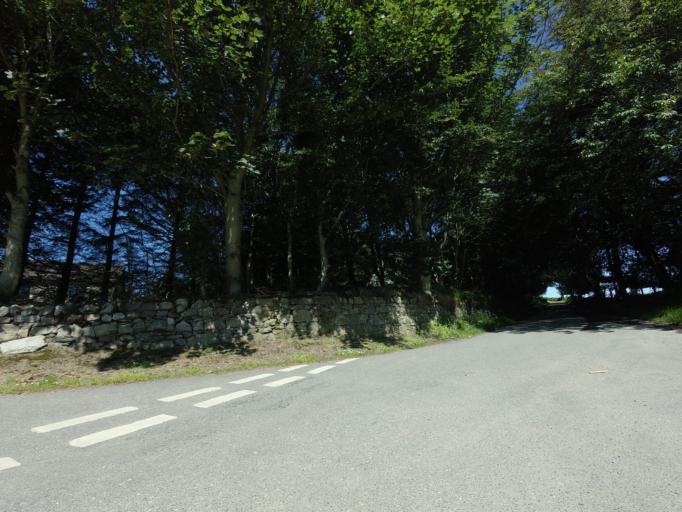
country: GB
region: Scotland
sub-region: Aberdeenshire
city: Macduff
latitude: 57.6440
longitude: -2.5079
